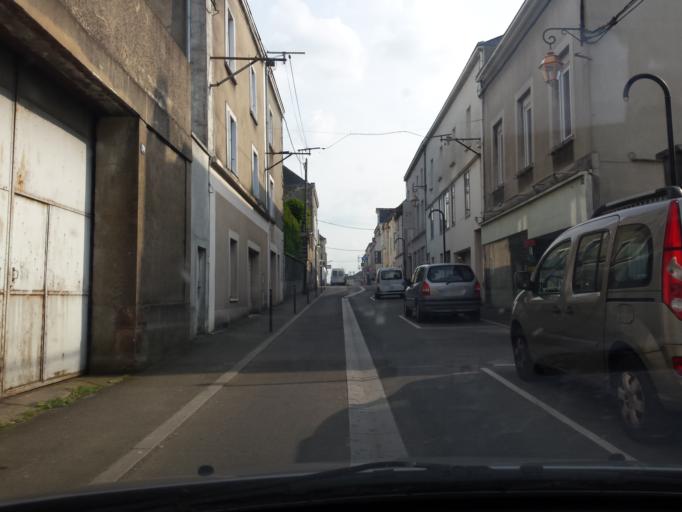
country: FR
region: Pays de la Loire
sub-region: Departement de Maine-et-Loire
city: Chemille-Melay
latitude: 47.2098
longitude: -0.7293
